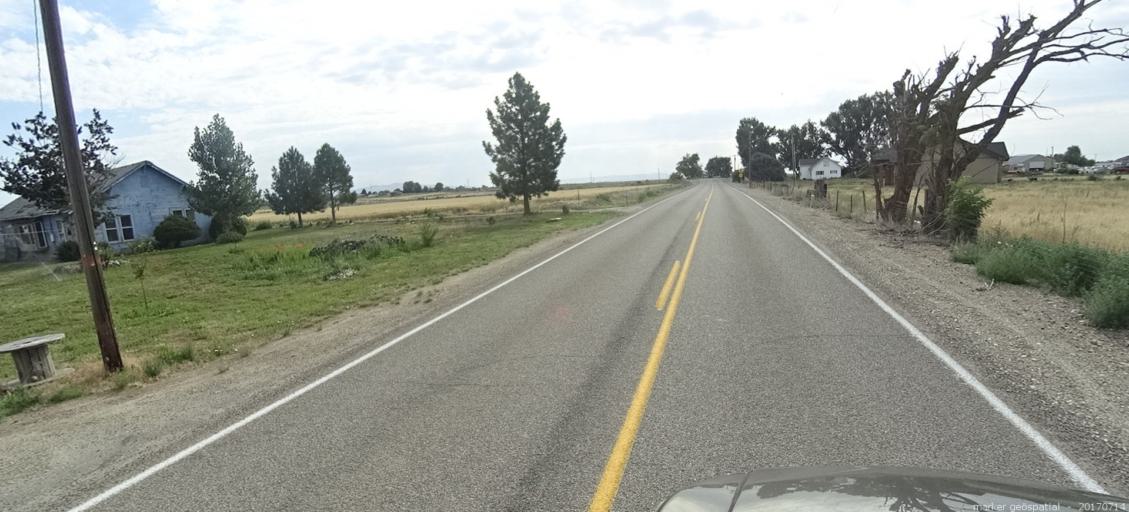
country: US
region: Idaho
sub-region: Ada County
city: Kuna
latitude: 43.4736
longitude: -116.3436
